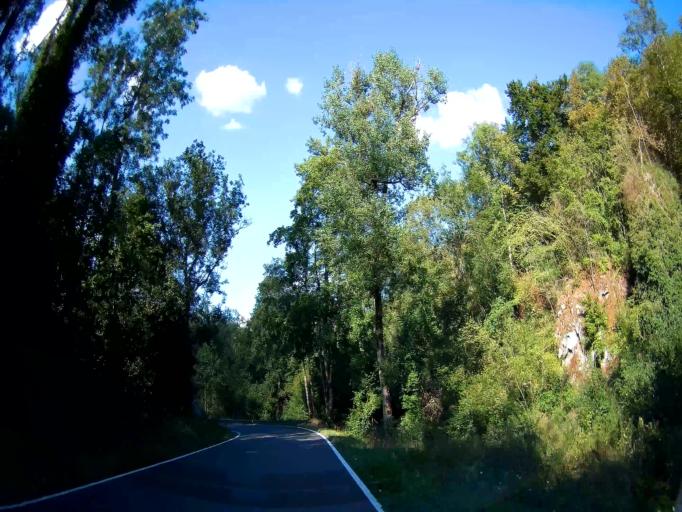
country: BE
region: Wallonia
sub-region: Province de Namur
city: Anhee
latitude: 50.2997
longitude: 4.8197
